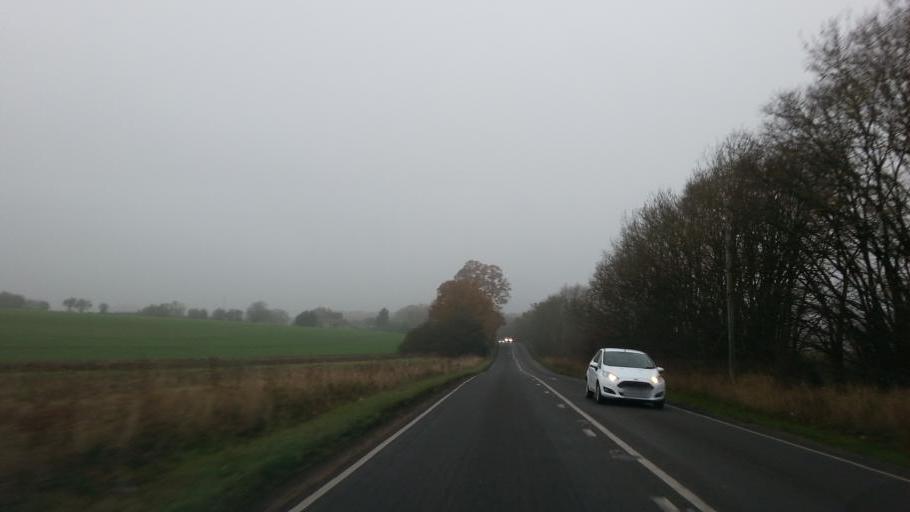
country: GB
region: England
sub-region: Cambridgeshire
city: Papworth Everard
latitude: 52.2360
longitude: -0.1084
